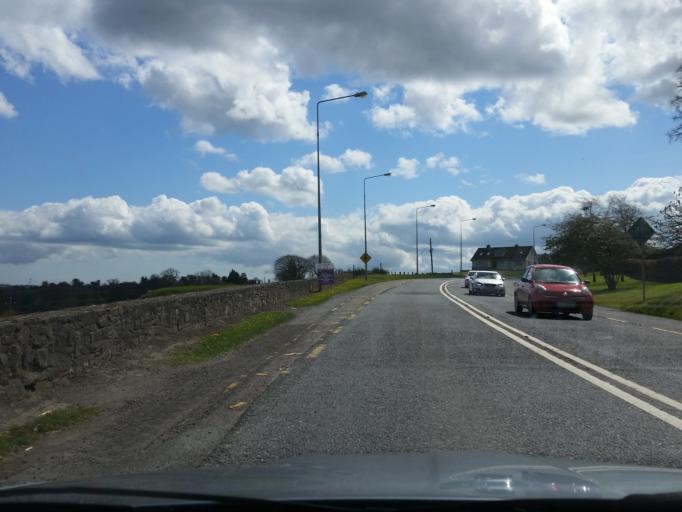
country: IE
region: Leinster
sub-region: An Mhi
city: Slane
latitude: 53.7008
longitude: -6.5392
